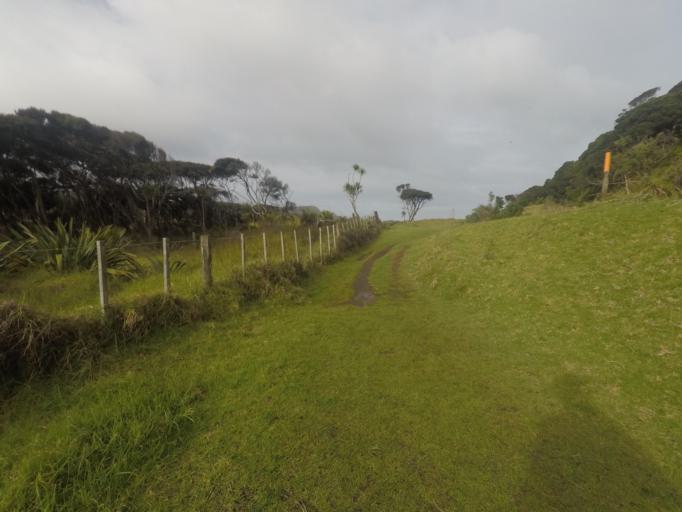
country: NZ
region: Auckland
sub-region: Auckland
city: Muriwai Beach
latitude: -36.8865
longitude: 174.4495
